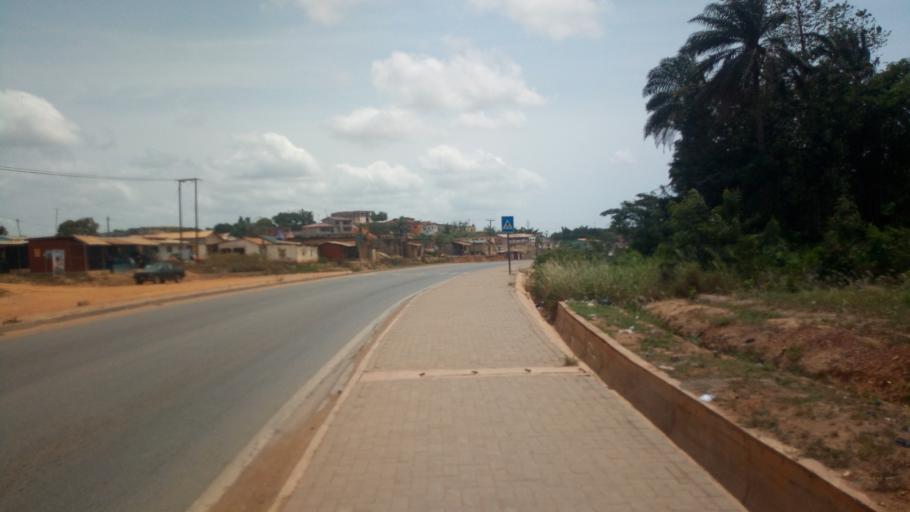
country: GH
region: Western
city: Sekondi-Takoradi
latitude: 4.9529
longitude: -1.7479
